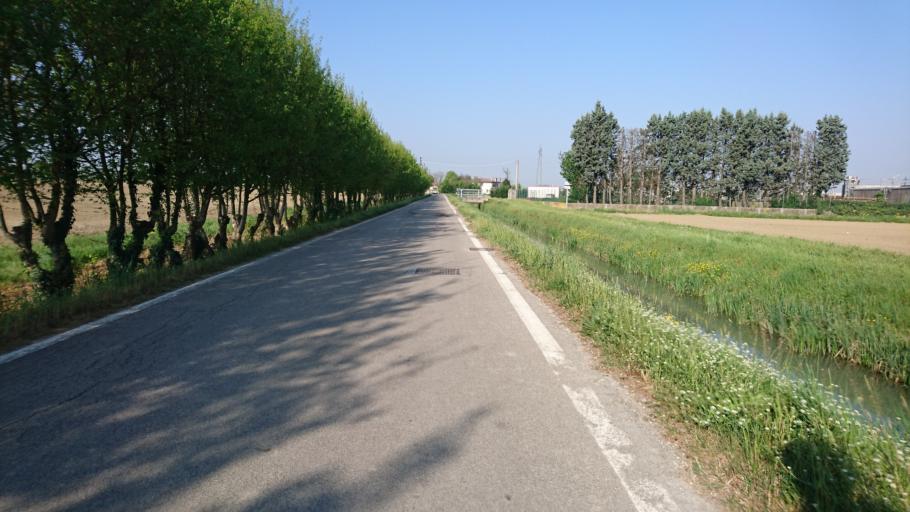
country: IT
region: Veneto
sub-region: Provincia di Treviso
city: Fornaci
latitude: 45.6447
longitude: 12.4313
